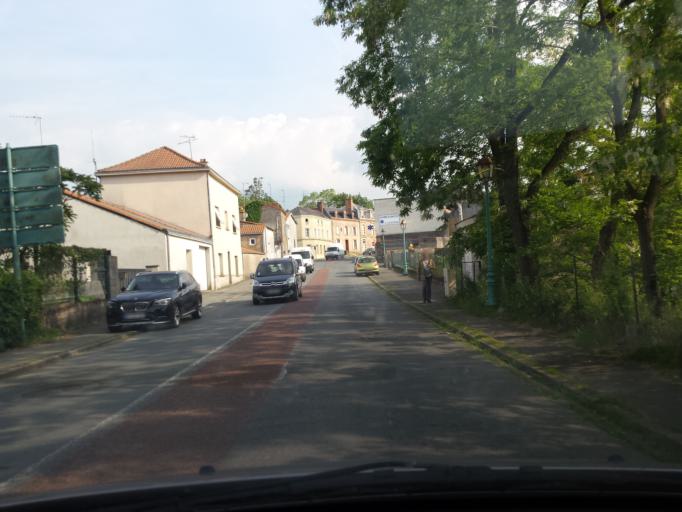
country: FR
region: Pays de la Loire
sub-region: Departement de Maine-et-Loire
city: Chemille-Melay
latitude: 47.2065
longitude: -0.7287
